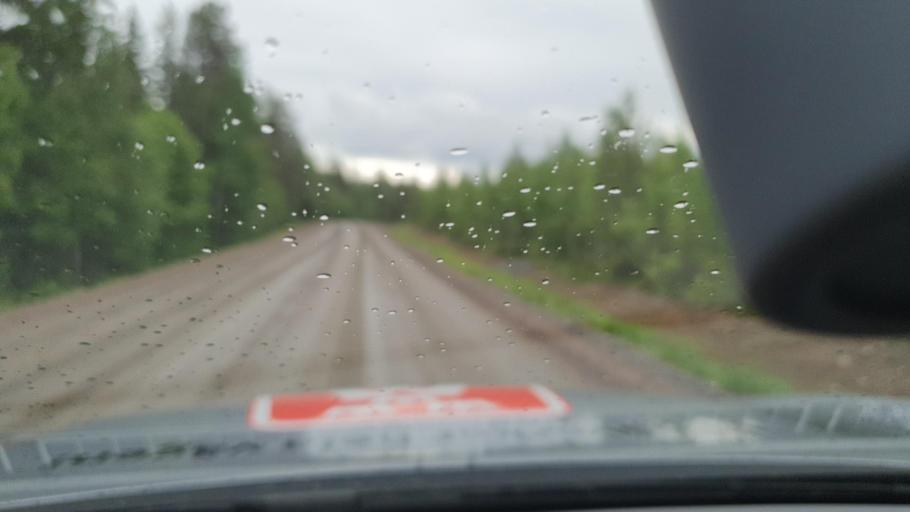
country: SE
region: Norrbotten
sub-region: Overtornea Kommun
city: OEvertornea
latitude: 66.4332
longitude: 23.5157
